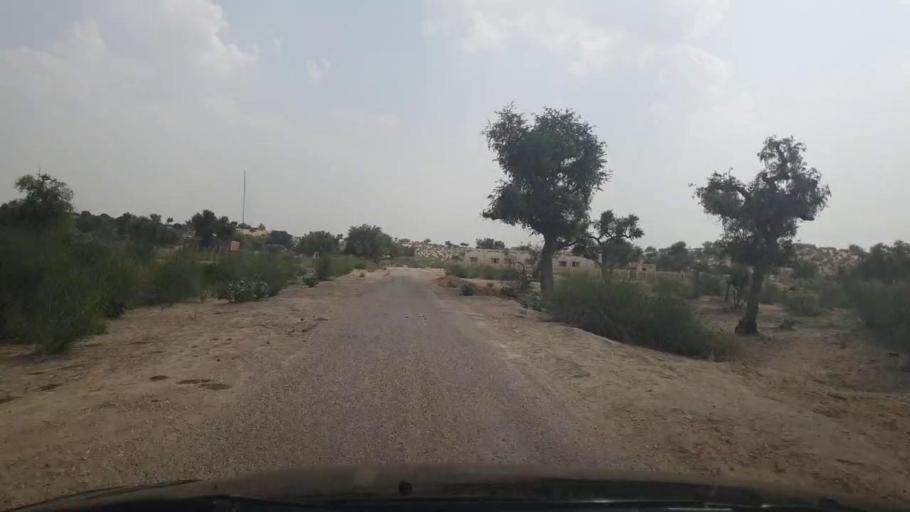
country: PK
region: Sindh
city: Islamkot
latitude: 24.9898
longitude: 70.4979
